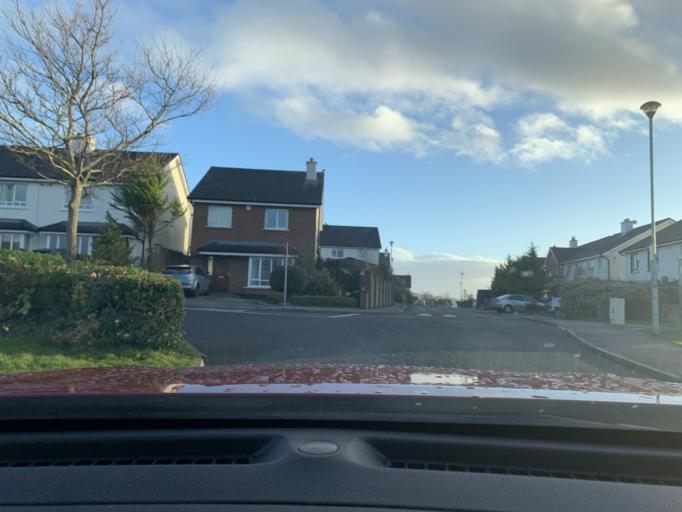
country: IE
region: Connaught
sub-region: Sligo
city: Sligo
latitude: 54.2517
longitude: -8.4681
